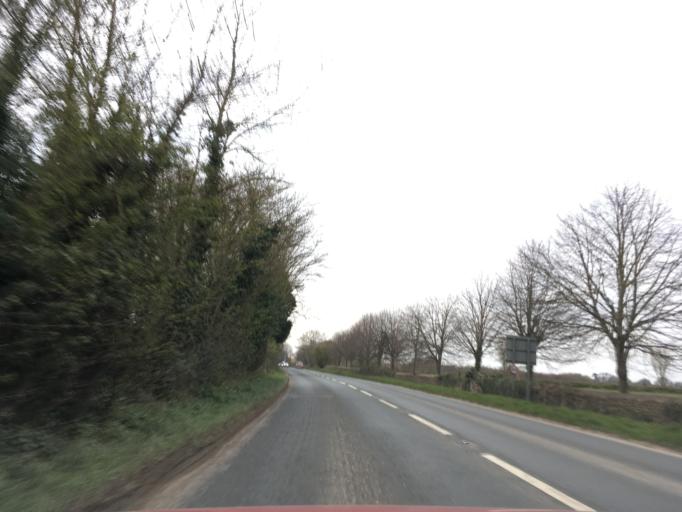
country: GB
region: England
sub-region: Gloucestershire
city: Tetbury
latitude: 51.6474
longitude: -2.1463
